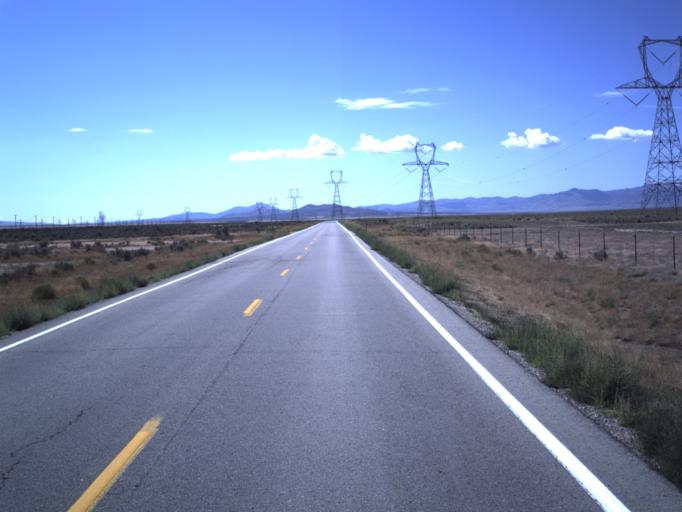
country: US
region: Utah
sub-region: Tooele County
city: Tooele
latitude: 40.2738
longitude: -112.3978
